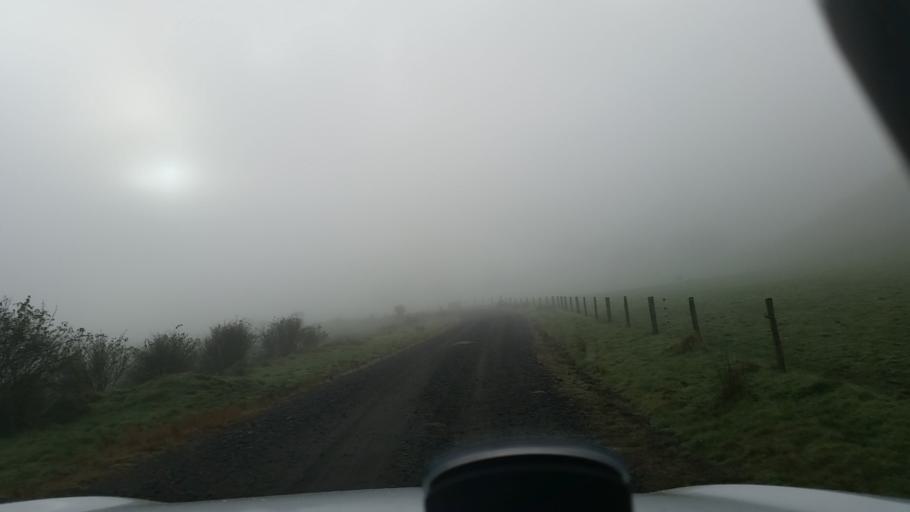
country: NZ
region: Taranaki
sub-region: South Taranaki District
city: Eltham
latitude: -39.4089
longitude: 174.4280
